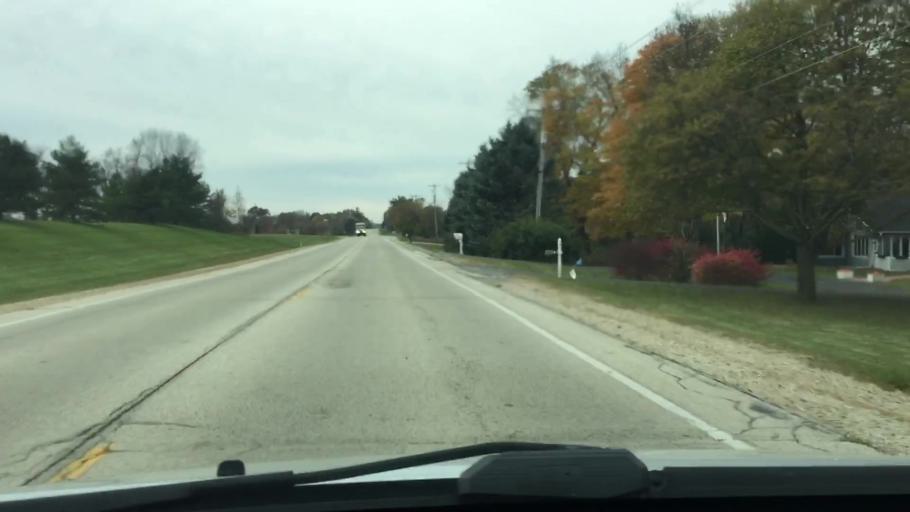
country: US
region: Wisconsin
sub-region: Waukesha County
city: Muskego
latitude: 42.9343
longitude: -88.1772
